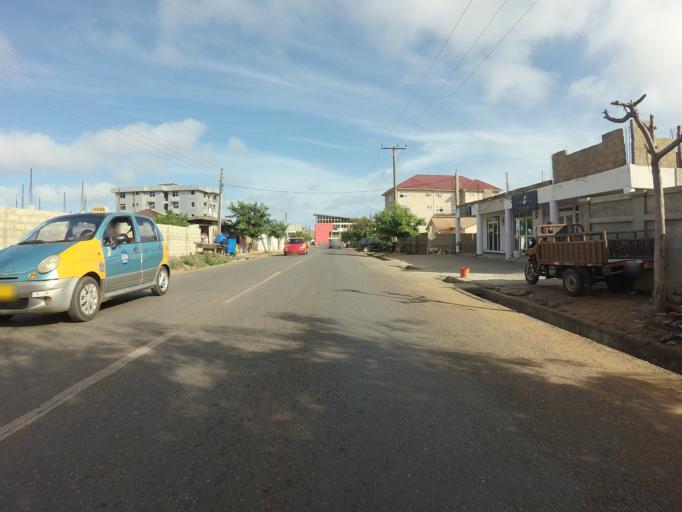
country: GH
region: Greater Accra
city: Teshi Old Town
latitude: 5.5768
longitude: -0.1391
